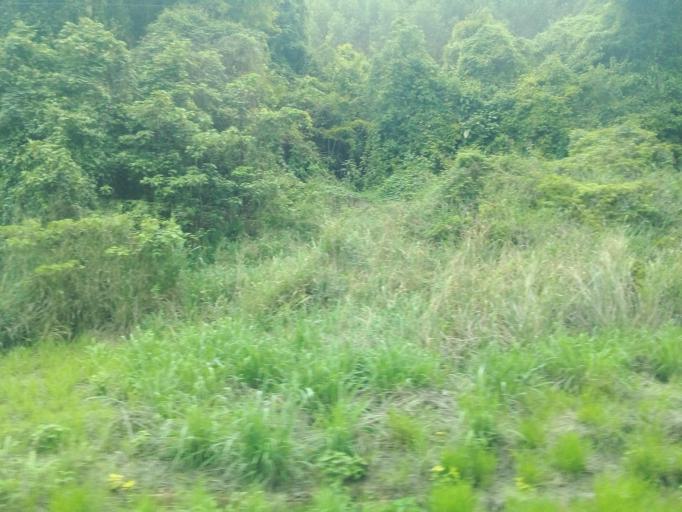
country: BR
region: Minas Gerais
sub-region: Nova Era
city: Nova Era
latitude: -19.7277
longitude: -42.9840
